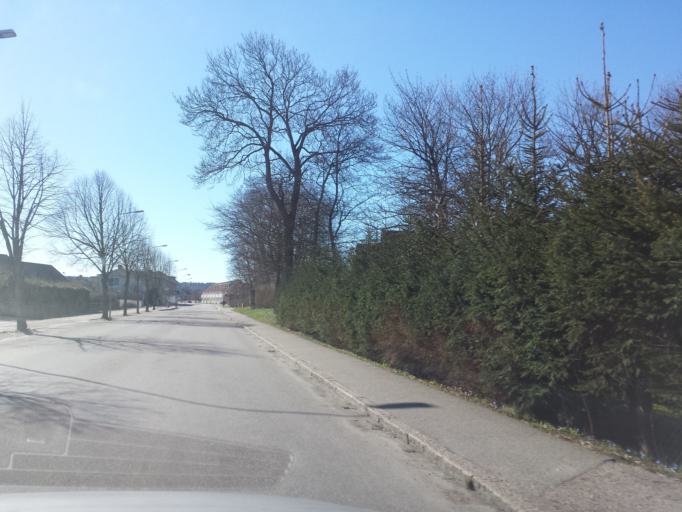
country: SE
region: Skane
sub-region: Sjobo Kommun
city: Sjoebo
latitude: 55.6401
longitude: 13.7054
